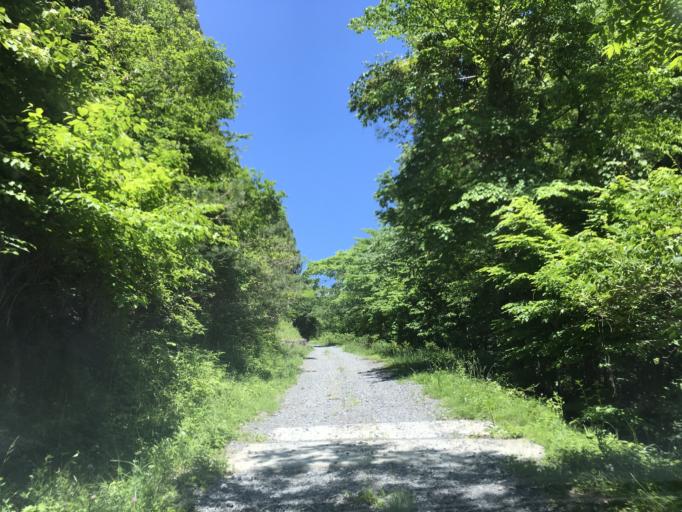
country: JP
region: Miyagi
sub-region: Oshika Gun
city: Onagawa Cho
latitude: 38.6867
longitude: 141.3506
